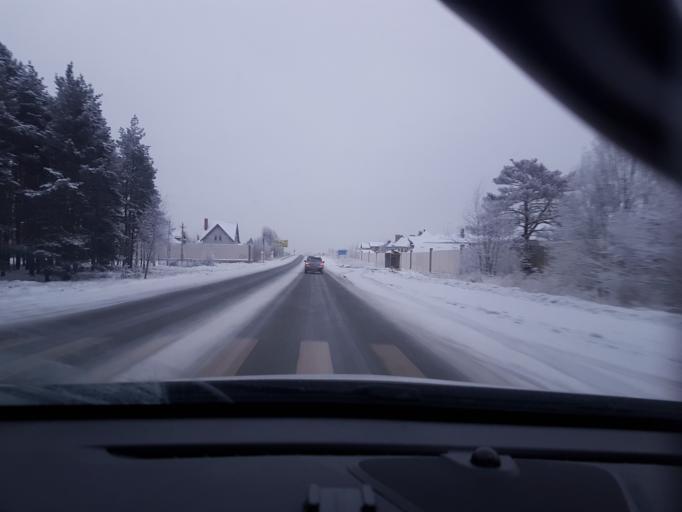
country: RU
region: Moskovskaya
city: Rozhdestveno
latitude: 55.8250
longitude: 37.0430
